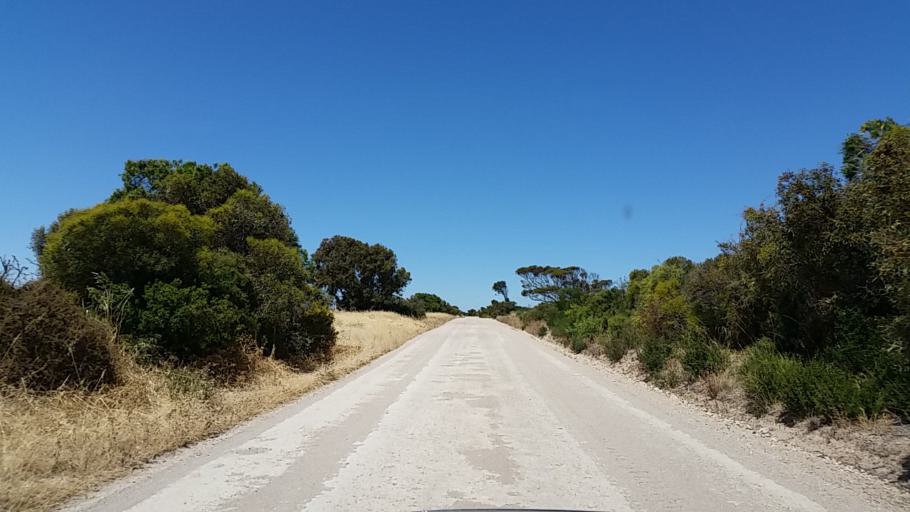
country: AU
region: South Australia
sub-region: Yorke Peninsula
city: Honiton
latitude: -35.0924
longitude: 137.4442
